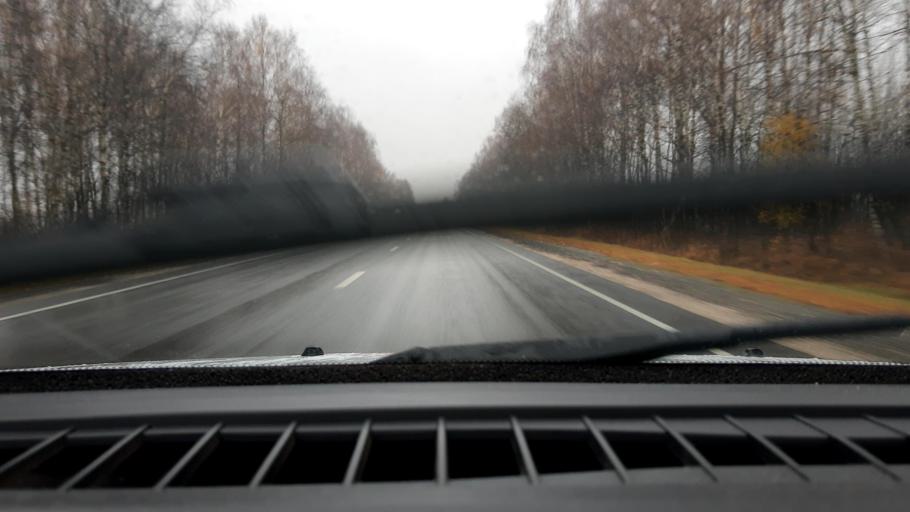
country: RU
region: Nizjnij Novgorod
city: Linda
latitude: 56.5507
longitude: 44.0213
